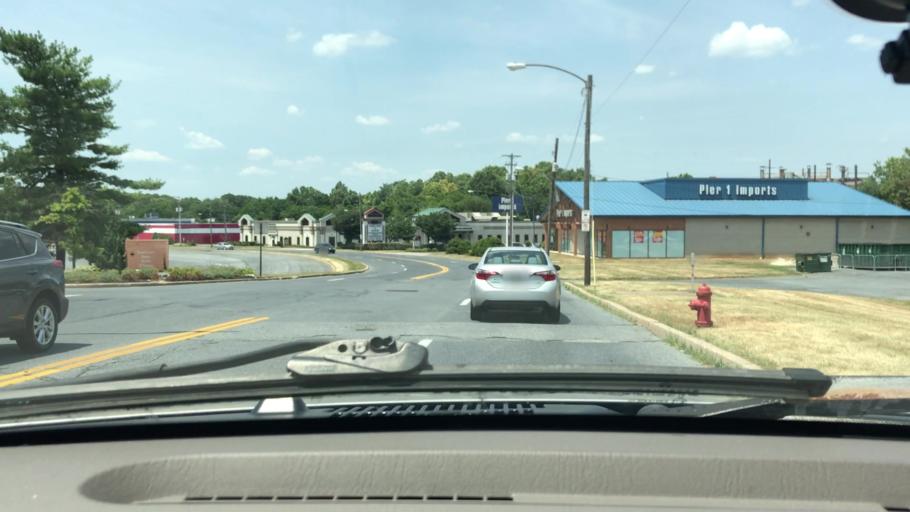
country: US
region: Pennsylvania
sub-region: Lancaster County
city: East Petersburg
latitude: 40.0701
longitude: -76.3388
